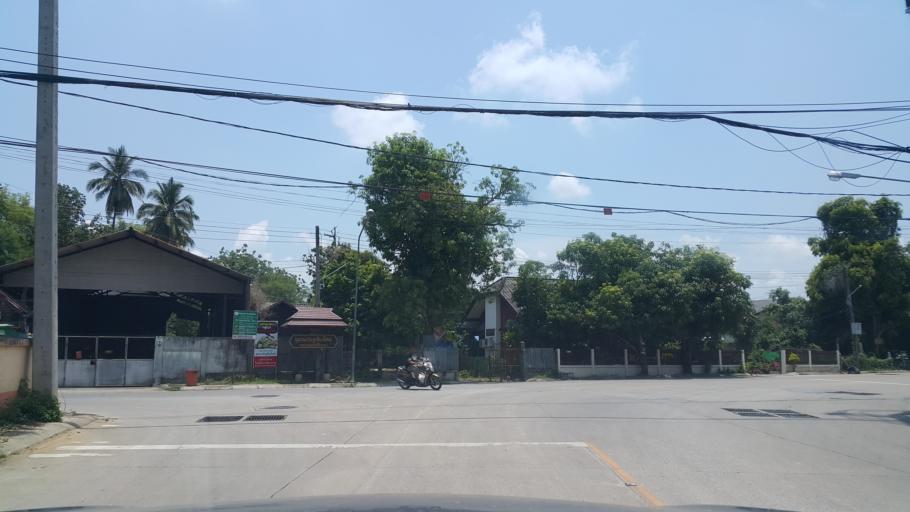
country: TH
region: Chiang Rai
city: Chiang Rai
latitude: 19.9085
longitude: 99.8220
